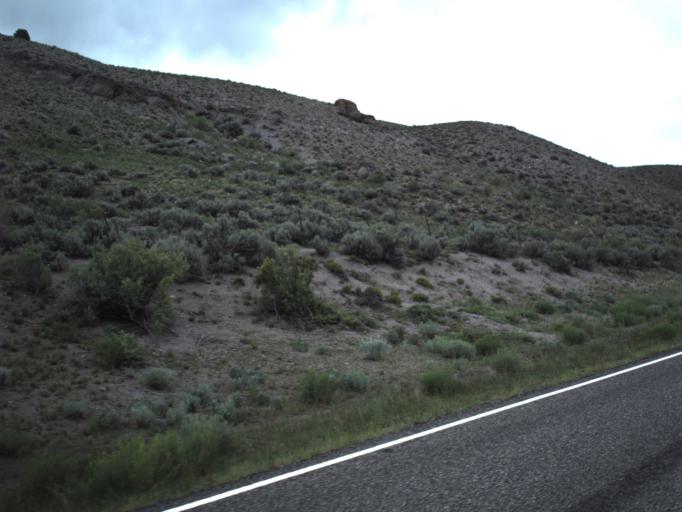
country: US
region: Utah
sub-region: Piute County
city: Junction
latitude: 38.1725
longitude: -112.0612
